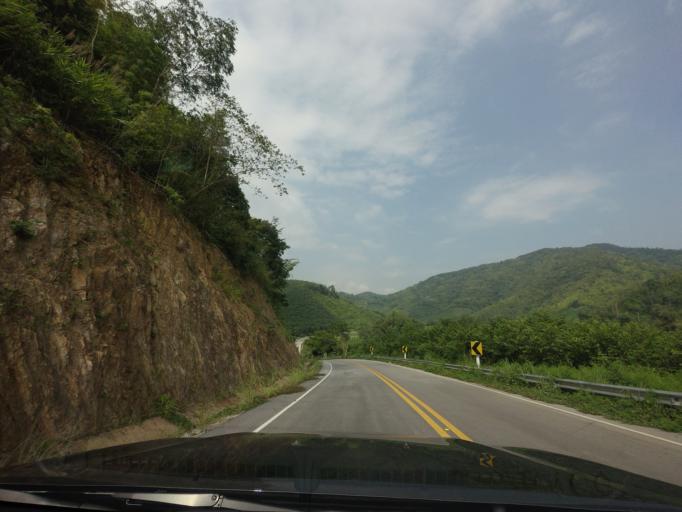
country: LA
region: Xiagnabouli
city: Muang Kenthao
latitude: 17.7736
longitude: 101.5288
